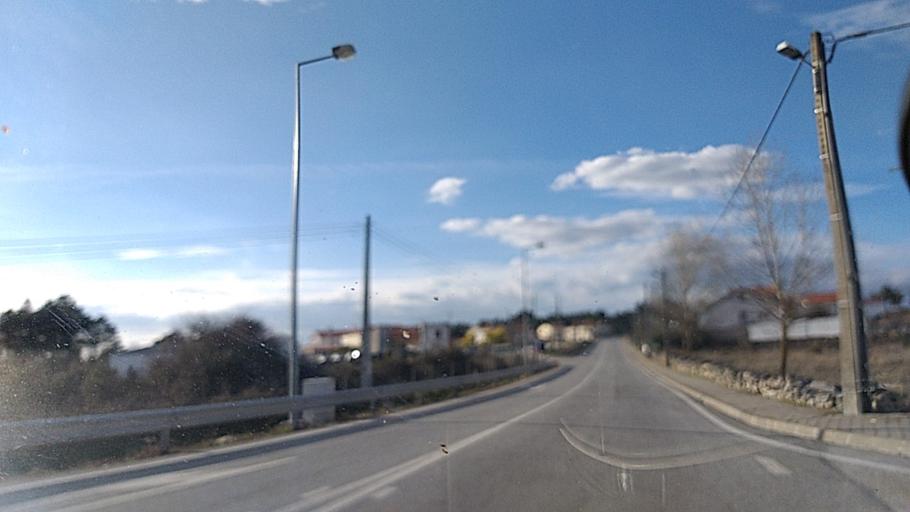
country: ES
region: Castille and Leon
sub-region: Provincia de Salamanca
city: Fuentes de Onoro
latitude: 40.6198
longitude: -6.8433
